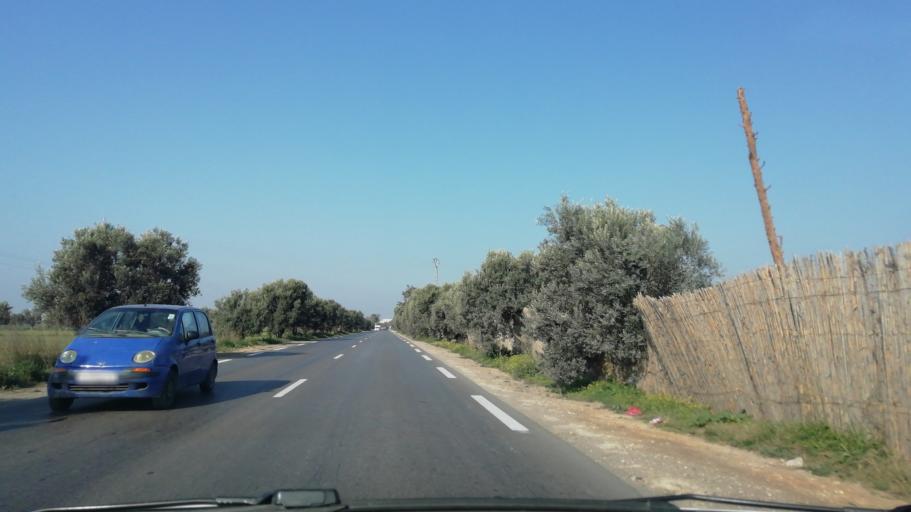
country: DZ
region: Mostaganem
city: Mostaganem
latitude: 35.7419
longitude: -0.0020
